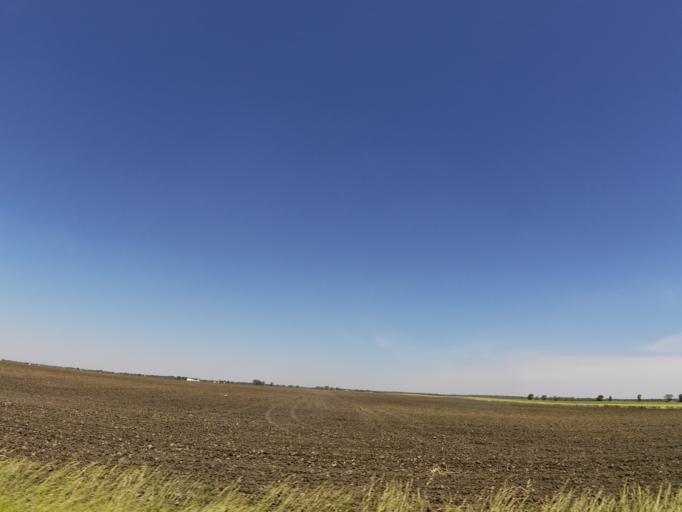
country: US
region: Illinois
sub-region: Iroquois County
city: Milford
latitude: 40.6318
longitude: -87.7446
